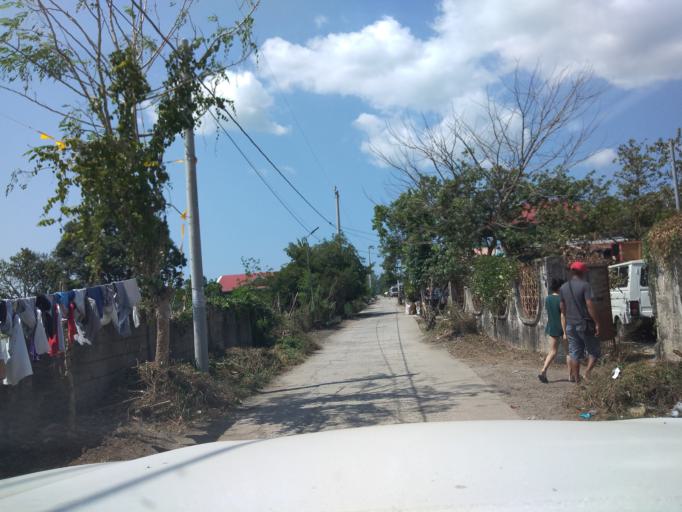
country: PH
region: Central Luzon
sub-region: Province of Pampanga
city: Bahay Pare
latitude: 15.0432
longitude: 120.8851
